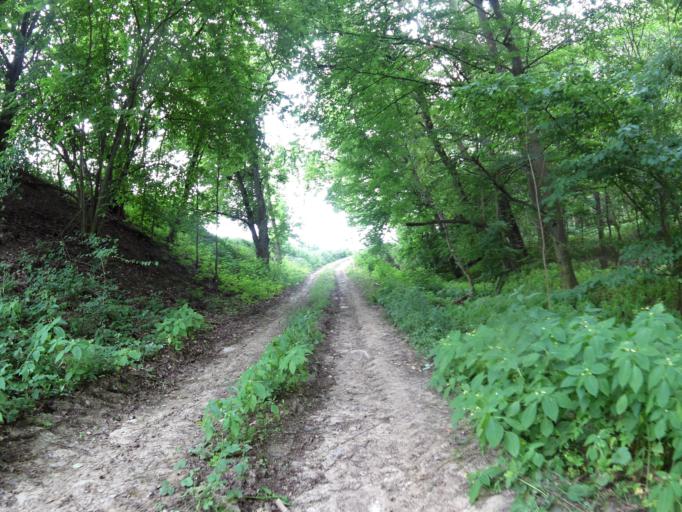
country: DE
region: Bavaria
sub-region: Regierungsbezirk Unterfranken
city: Geroldshausen
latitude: 49.7105
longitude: 9.8892
